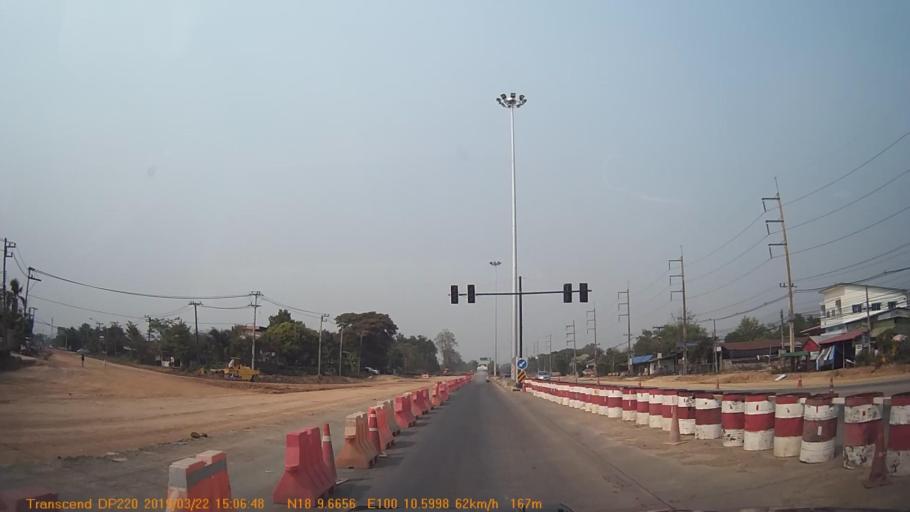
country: TH
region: Phrae
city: Phrae
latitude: 18.1612
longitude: 100.1767
